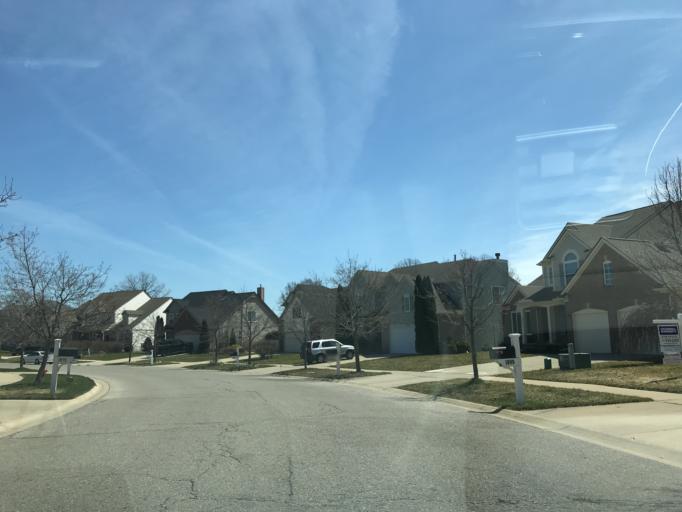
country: US
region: Michigan
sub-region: Washtenaw County
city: Ann Arbor
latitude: 42.2570
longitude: -83.7860
